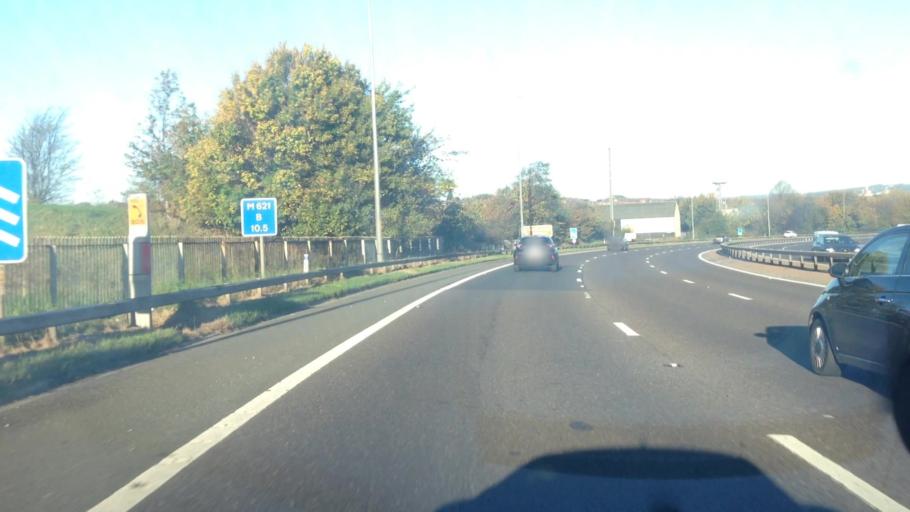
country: GB
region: England
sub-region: City and Borough of Leeds
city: Leeds
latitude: 53.7711
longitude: -1.5384
